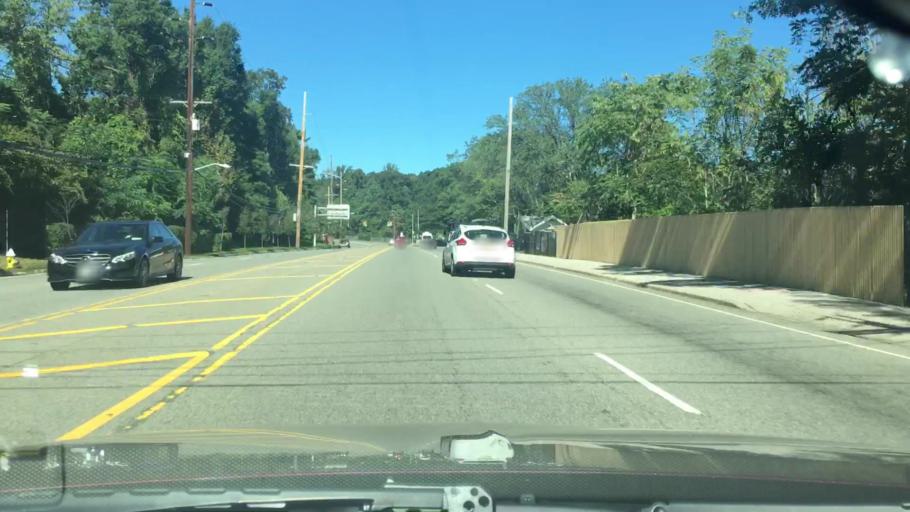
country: US
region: New York
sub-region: Nassau County
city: Searingtown
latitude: 40.7826
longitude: -73.6629
